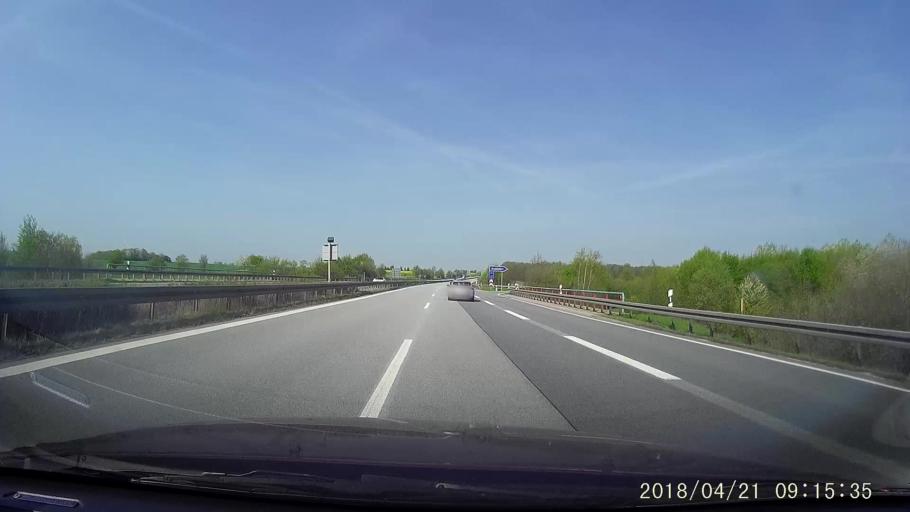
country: DE
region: Saxony
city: Reichenbach
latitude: 51.2031
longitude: 14.7605
